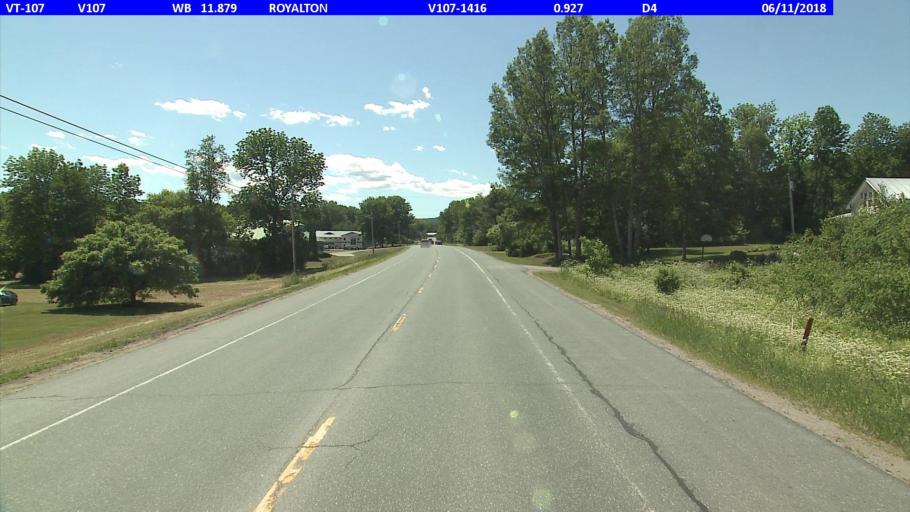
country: US
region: Vermont
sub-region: Orange County
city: Randolph
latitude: 43.8237
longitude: -72.5967
